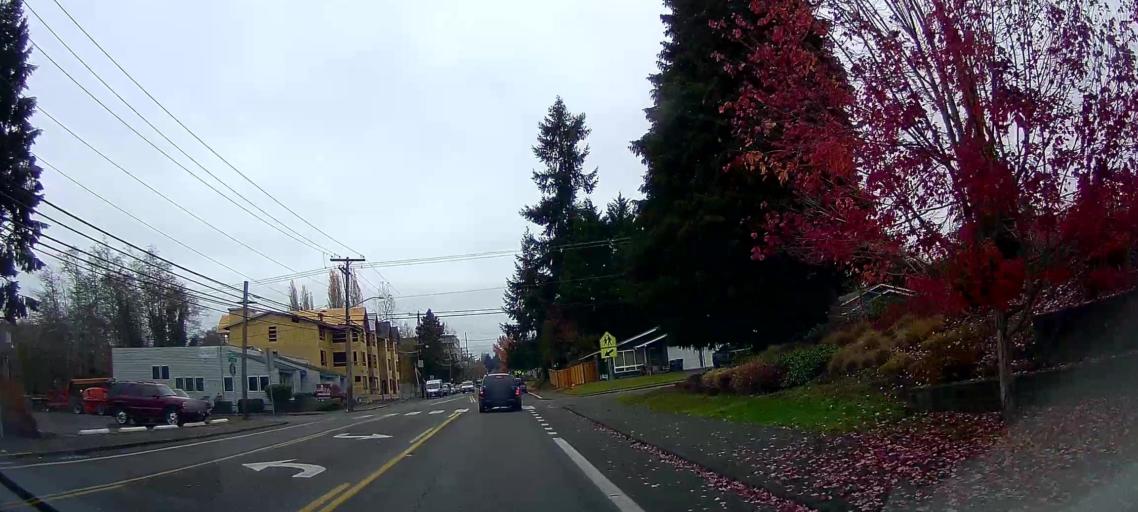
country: US
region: Washington
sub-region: Thurston County
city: Olympia
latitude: 47.0404
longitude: -122.8876
